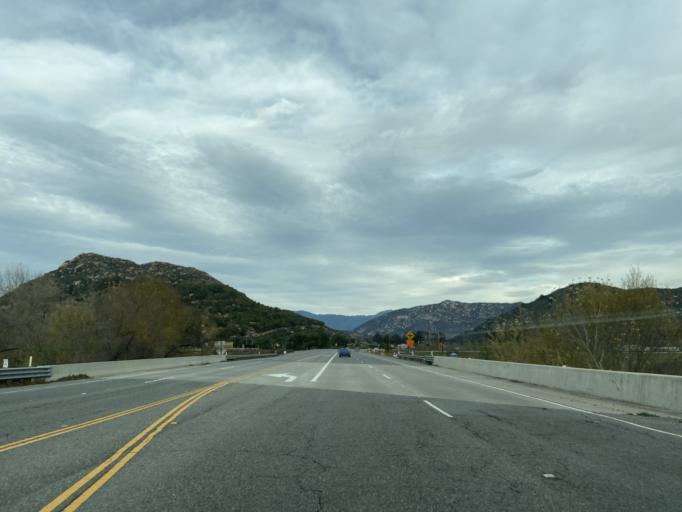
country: US
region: California
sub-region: San Diego County
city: Rainbow
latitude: 33.3351
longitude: -117.1535
